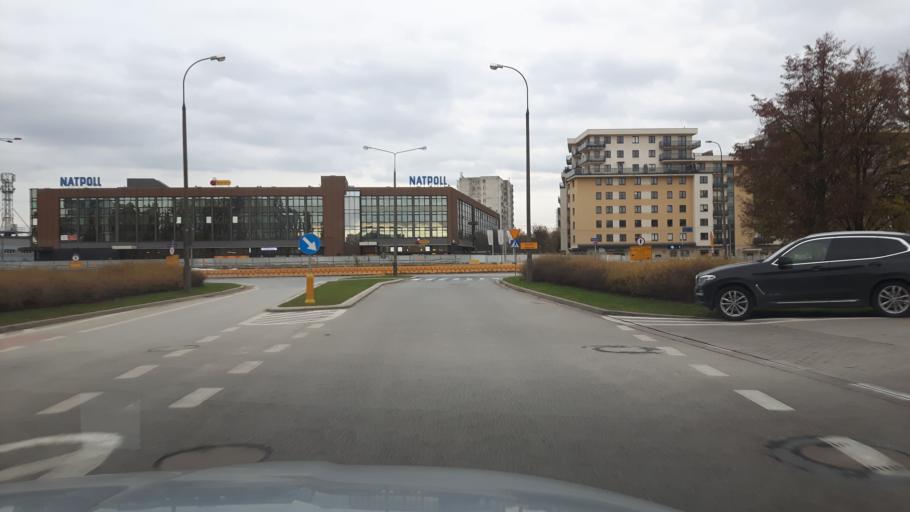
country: PL
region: Masovian Voivodeship
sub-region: Warszawa
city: Ursynow
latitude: 52.1485
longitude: 21.0564
